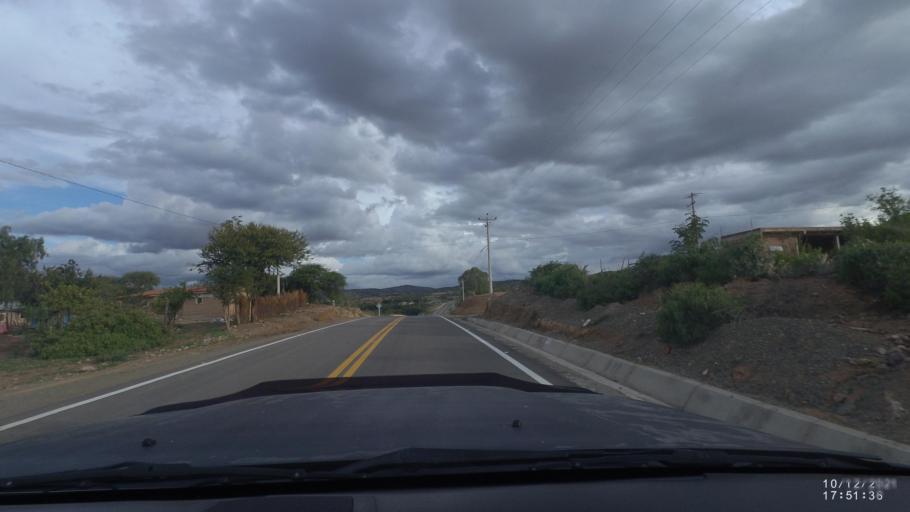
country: BO
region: Cochabamba
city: Tarata
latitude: -17.6784
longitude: -65.9581
